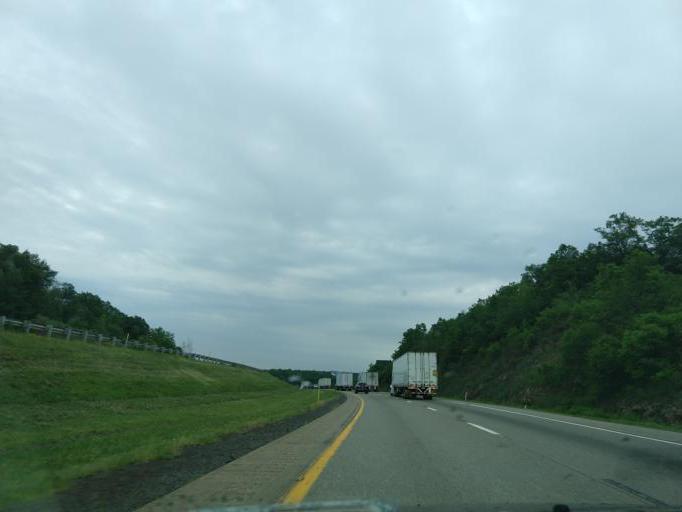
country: US
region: Pennsylvania
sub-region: Luzerne County
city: Conyngham
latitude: 40.9804
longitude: -76.0359
